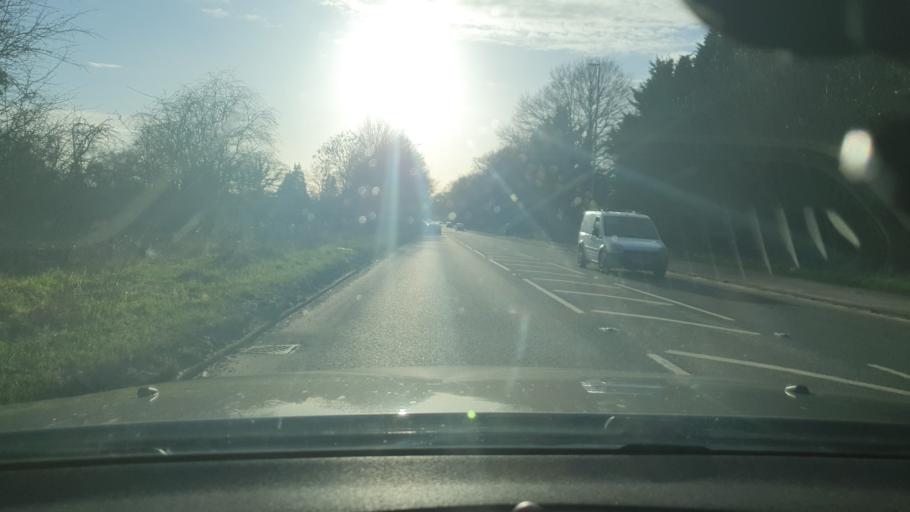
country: GB
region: England
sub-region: Wokingham
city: Charvil
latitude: 51.4852
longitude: -0.8739
